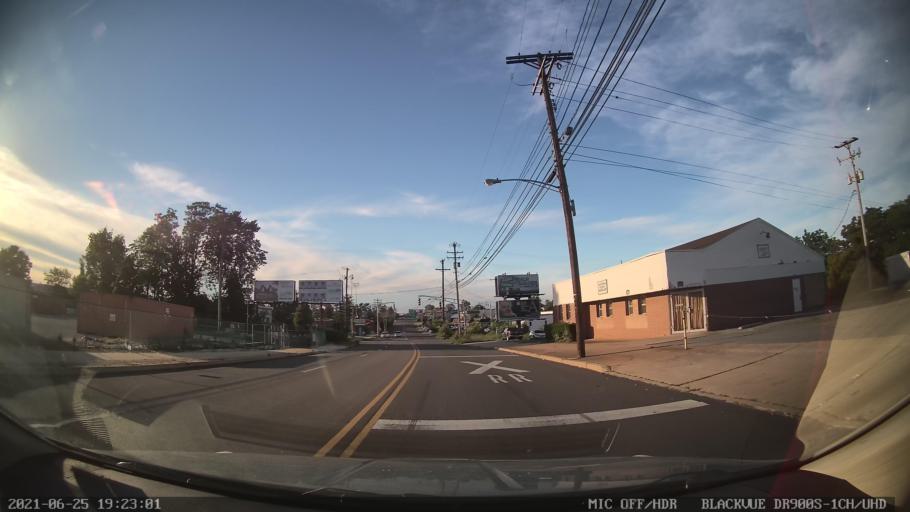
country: US
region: Pennsylvania
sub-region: Berks County
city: Hyde Park
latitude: 40.3633
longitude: -75.9325
